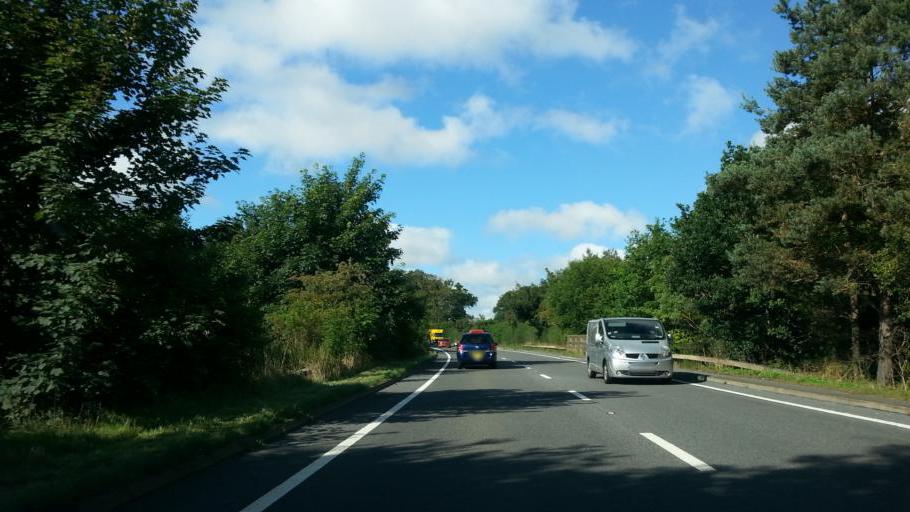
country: GB
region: England
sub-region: Northamptonshire
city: Broughton
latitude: 52.3782
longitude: -0.7785
